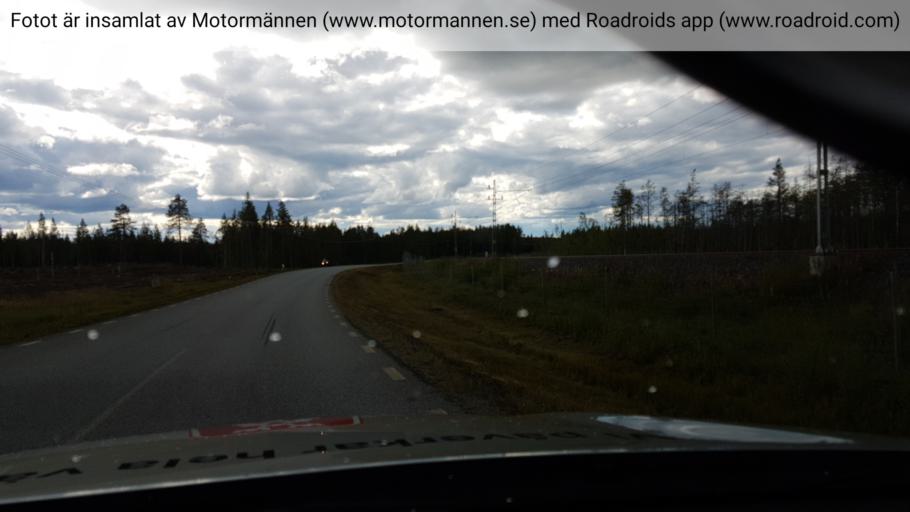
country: SE
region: Norrbotten
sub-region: Lulea Kommun
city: Ranea
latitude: 66.0410
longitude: 22.3369
